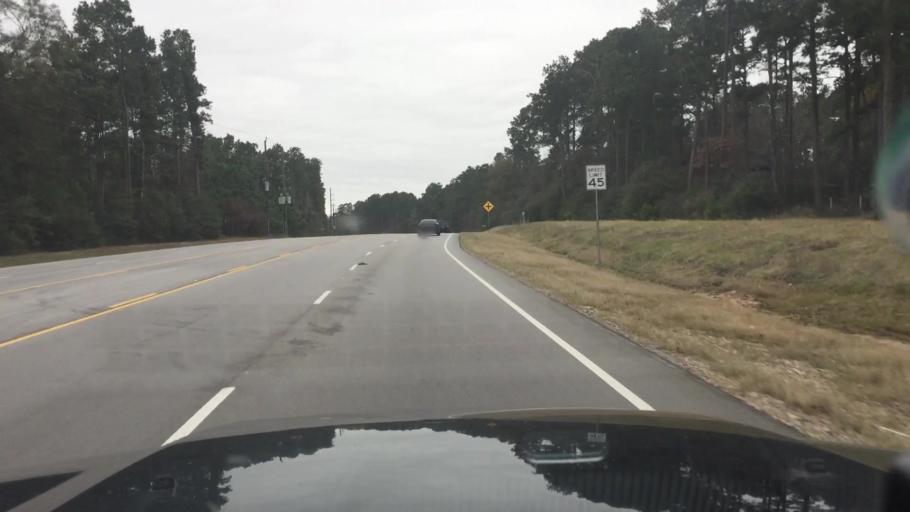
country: US
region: Texas
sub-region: Montgomery County
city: The Woodlands
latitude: 30.2457
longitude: -95.5648
